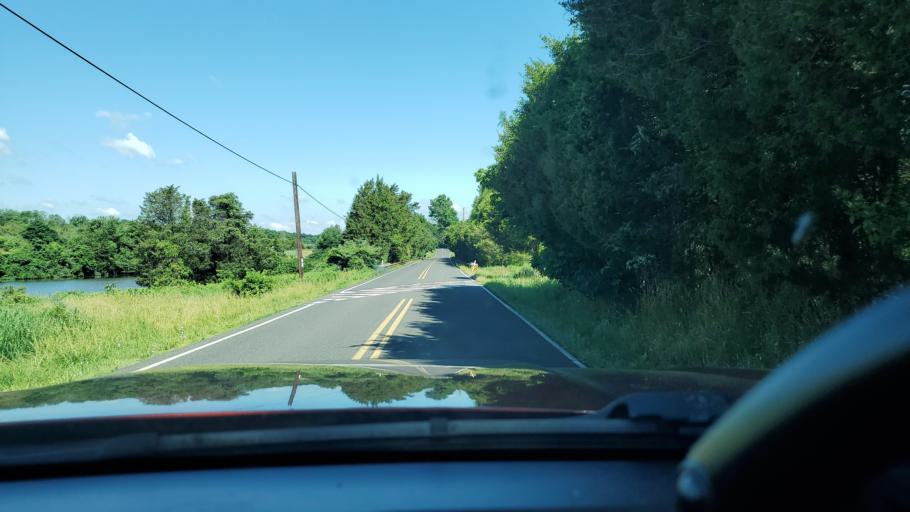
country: US
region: Pennsylvania
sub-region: Montgomery County
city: Red Hill
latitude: 40.3582
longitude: -75.5004
